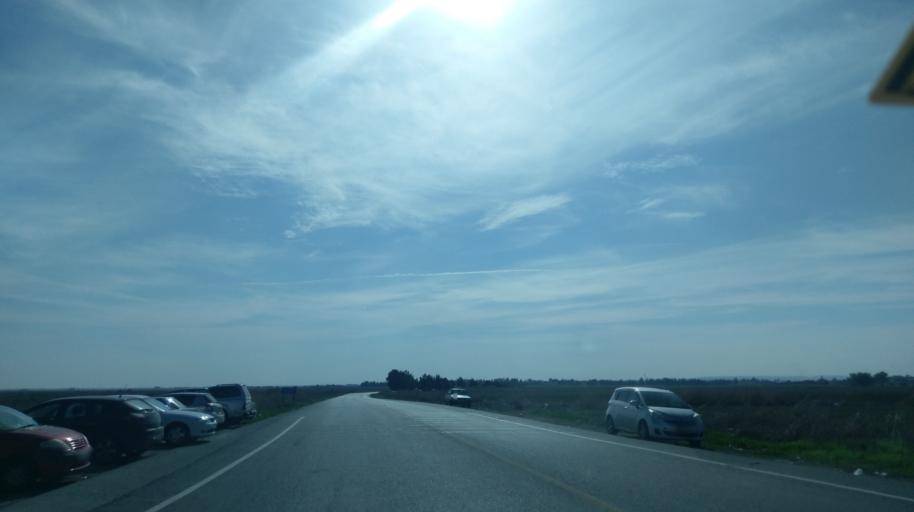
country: CY
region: Ammochostos
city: Lefkonoiko
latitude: 35.1822
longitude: 33.7011
